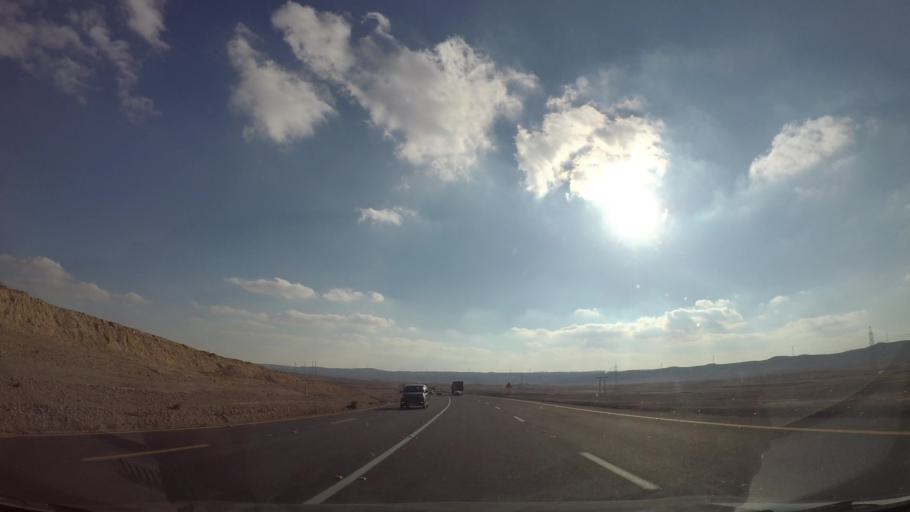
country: JO
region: Karak
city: Karak City
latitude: 31.1255
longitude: 36.0171
